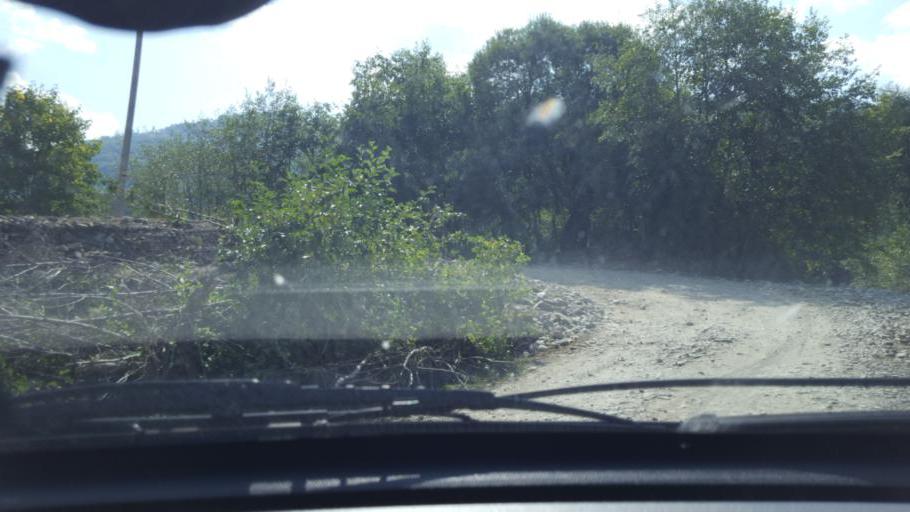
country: ME
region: Andrijevica
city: Andrijevica
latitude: 42.5937
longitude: 19.6800
